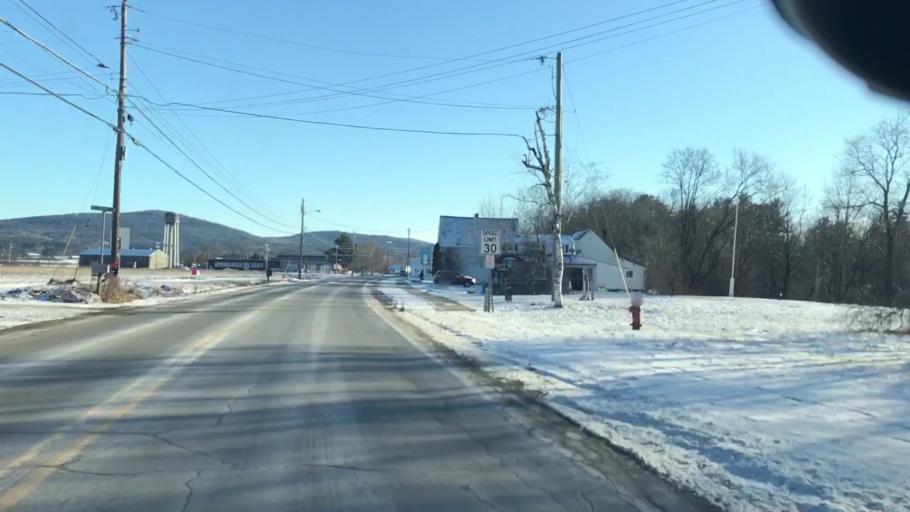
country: US
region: New Hampshire
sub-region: Grafton County
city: North Haverhill
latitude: 44.1002
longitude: -72.0261
